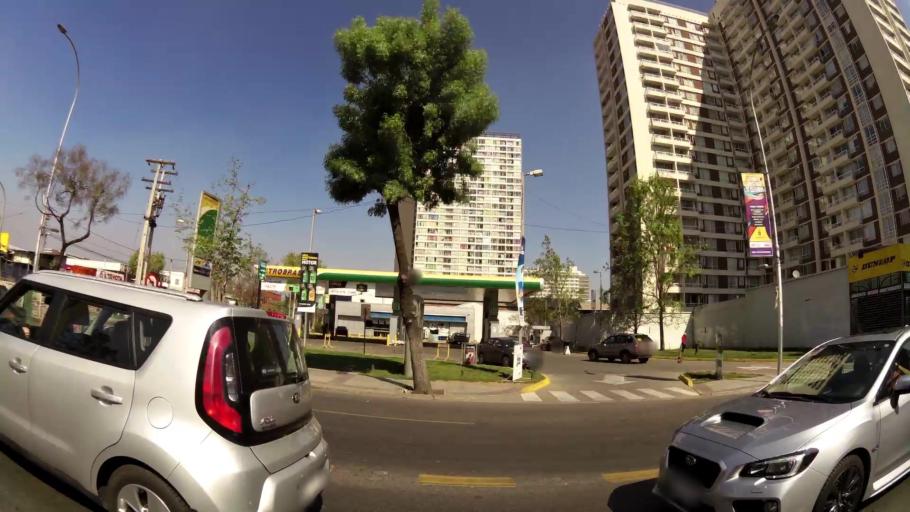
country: CL
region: Santiago Metropolitan
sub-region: Provincia de Santiago
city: Santiago
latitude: -33.4556
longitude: -70.6303
